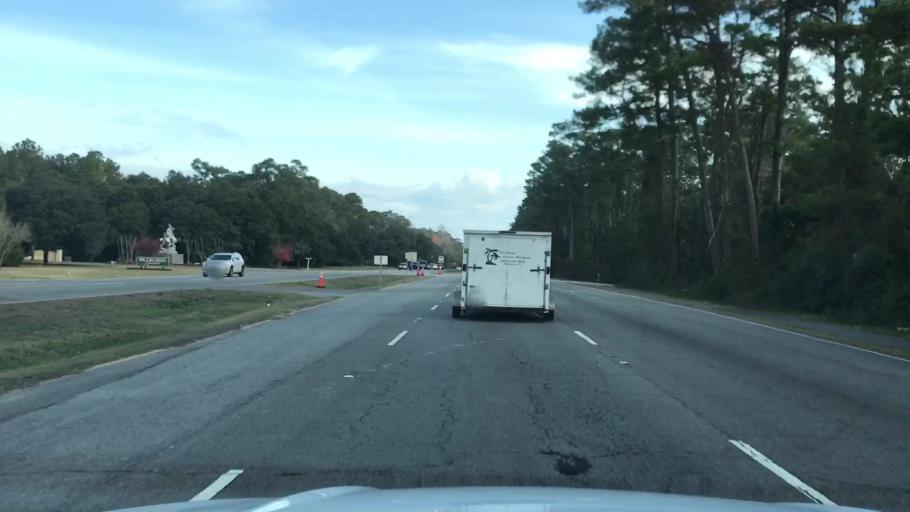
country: US
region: South Carolina
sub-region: Georgetown County
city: Murrells Inlet
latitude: 33.5081
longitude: -79.0774
